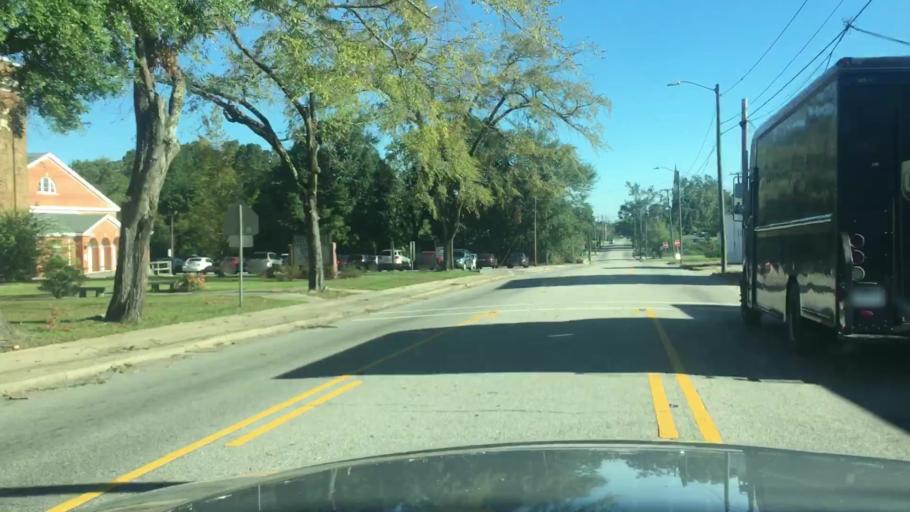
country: US
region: North Carolina
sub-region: Cumberland County
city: Fayetteville
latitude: 35.0307
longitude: -78.8945
